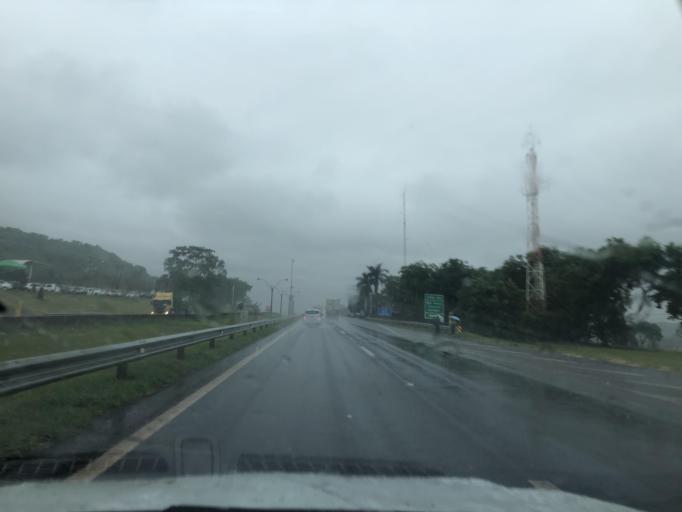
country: BR
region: Sao Paulo
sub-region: Ribeirao Preto
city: Ribeirao Preto
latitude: -21.2281
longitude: -47.7596
